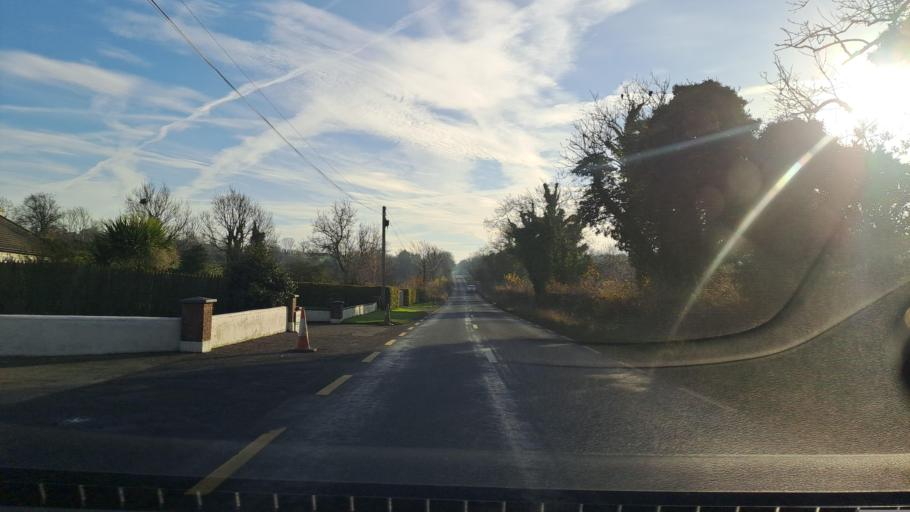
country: IE
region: Ulster
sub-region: An Cabhan
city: Kingscourt
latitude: 53.8928
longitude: -6.7576
